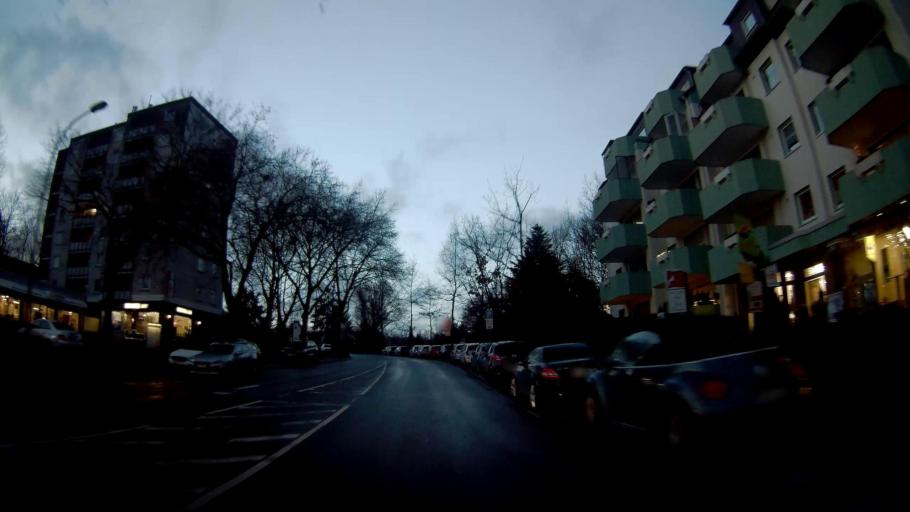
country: DE
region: North Rhine-Westphalia
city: Castrop-Rauxel
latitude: 51.5003
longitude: 7.2815
